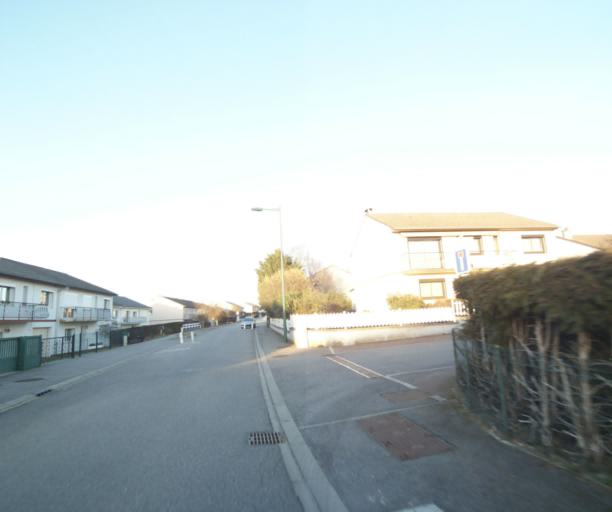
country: FR
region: Lorraine
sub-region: Departement de Meurthe-et-Moselle
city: Saulxures-les-Nancy
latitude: 48.6869
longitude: 6.2361
